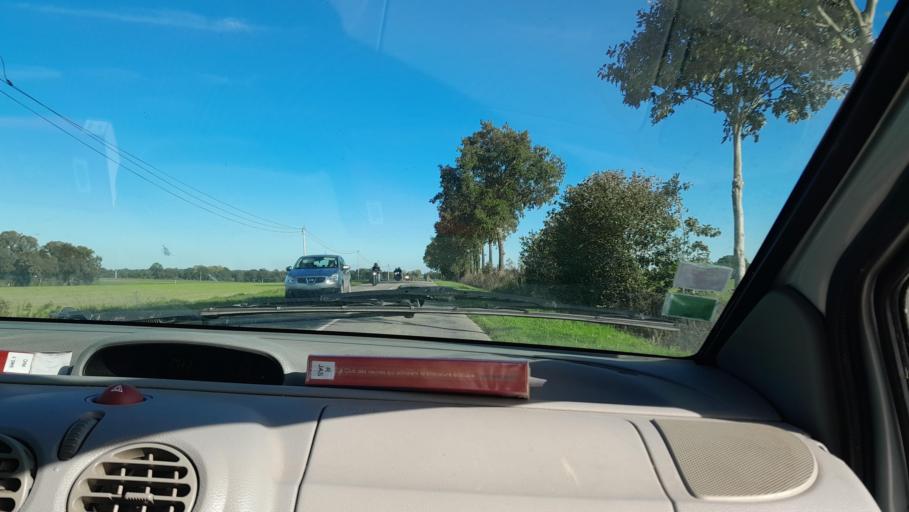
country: FR
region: Brittany
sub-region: Departement d'Ille-et-Vilaine
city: Le Pertre
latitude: 47.9685
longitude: -1.0857
